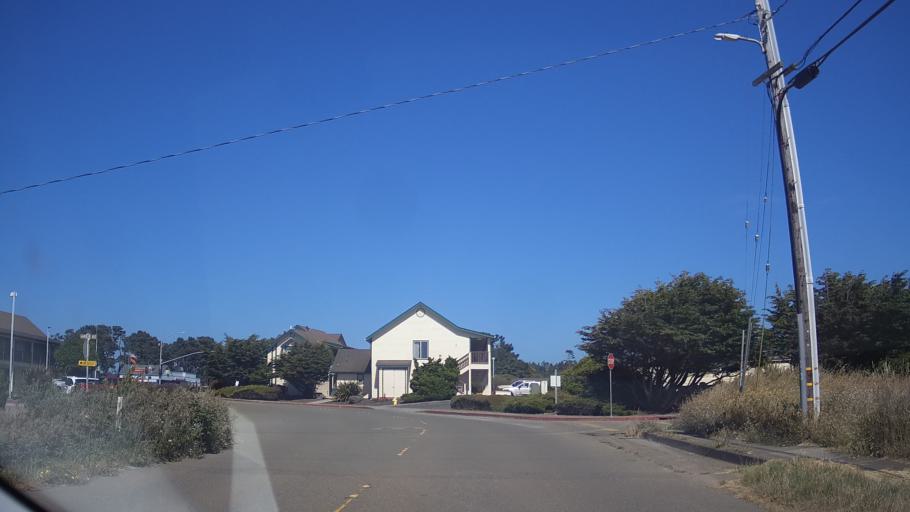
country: US
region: California
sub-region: Mendocino County
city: Fort Bragg
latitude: 39.4233
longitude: -123.8093
